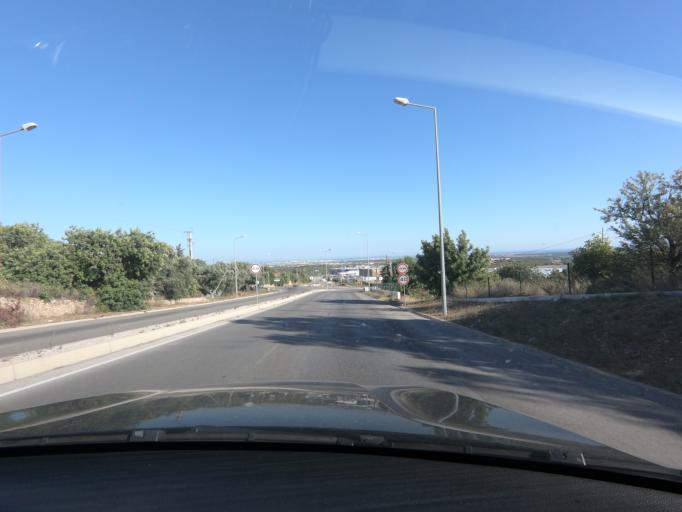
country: PT
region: Faro
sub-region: Faro
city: Santa Barbara de Nexe
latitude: 37.1040
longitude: -7.9998
